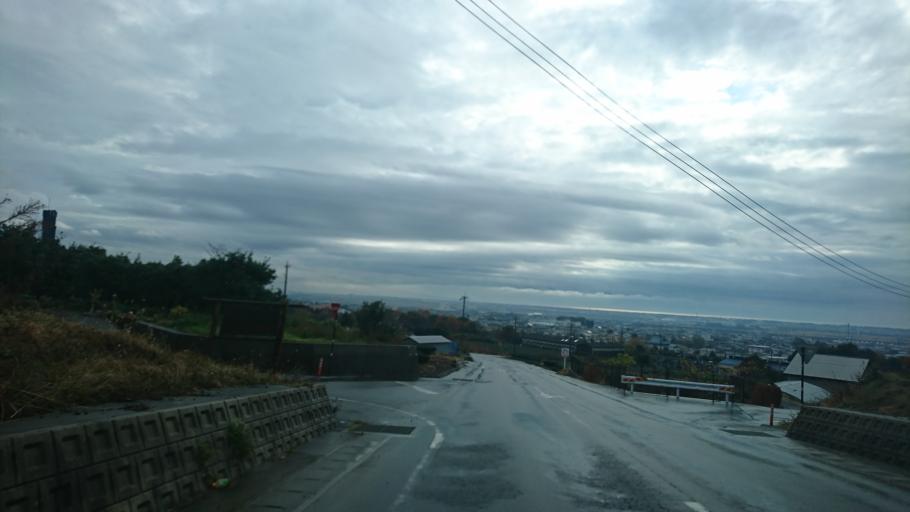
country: JP
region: Shizuoka
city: Fuji
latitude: 35.1695
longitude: 138.7345
